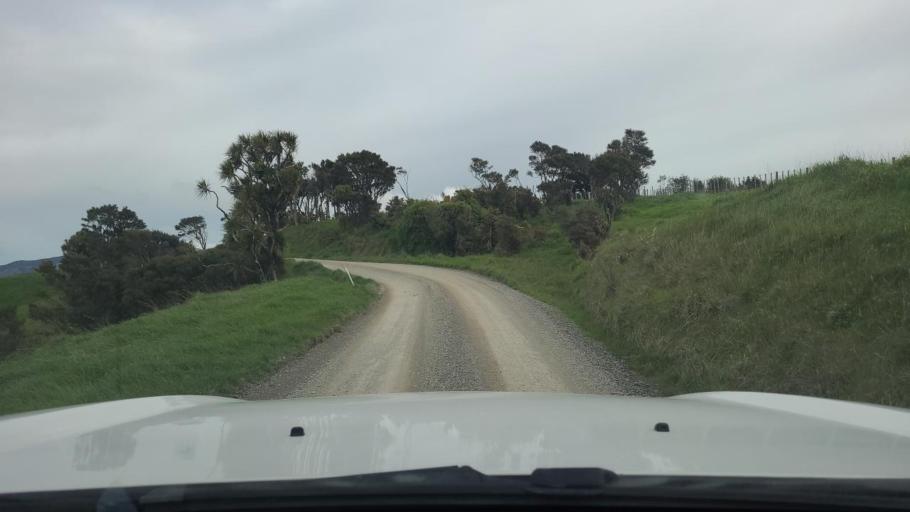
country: NZ
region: Wellington
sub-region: South Wairarapa District
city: Waipawa
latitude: -41.3682
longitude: 175.4792
